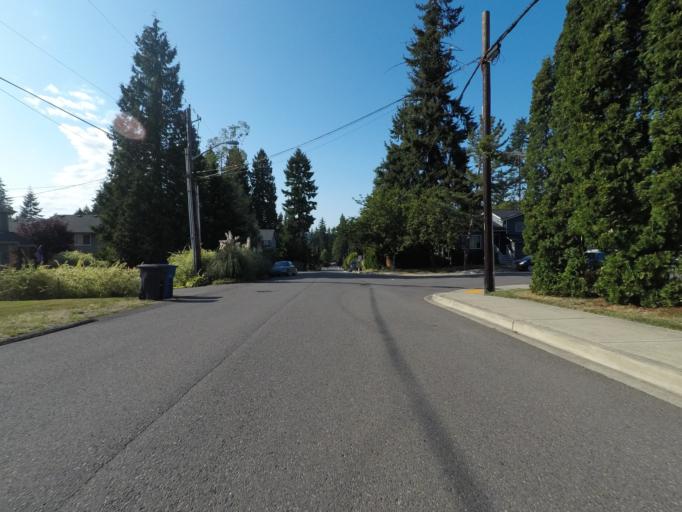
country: US
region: Washington
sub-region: King County
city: Kenmore
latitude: 47.7453
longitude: -122.2341
